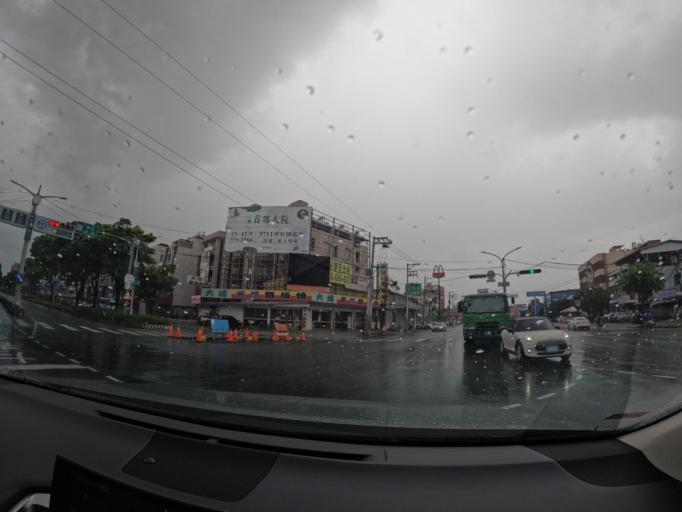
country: TW
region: Taiwan
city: Fengshan
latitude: 22.6591
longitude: 120.3642
